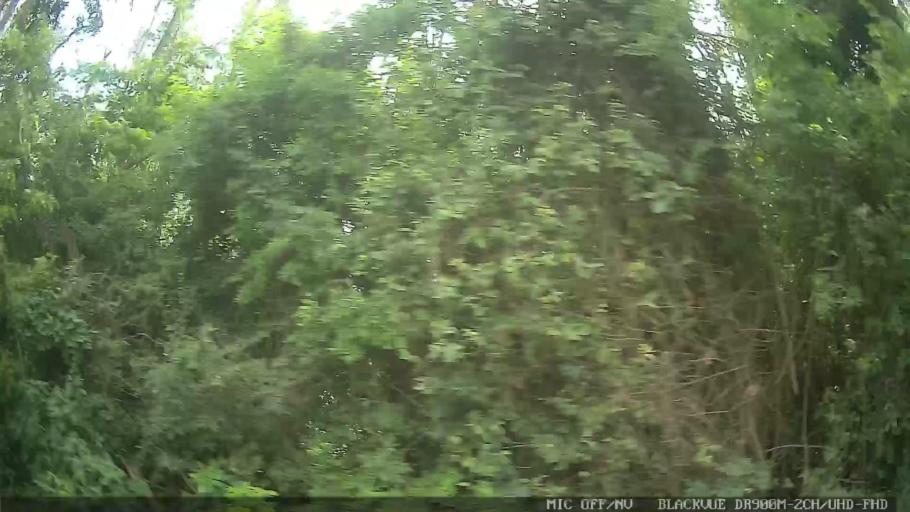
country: BR
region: Sao Paulo
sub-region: Conchas
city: Conchas
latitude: -23.0581
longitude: -47.9804
